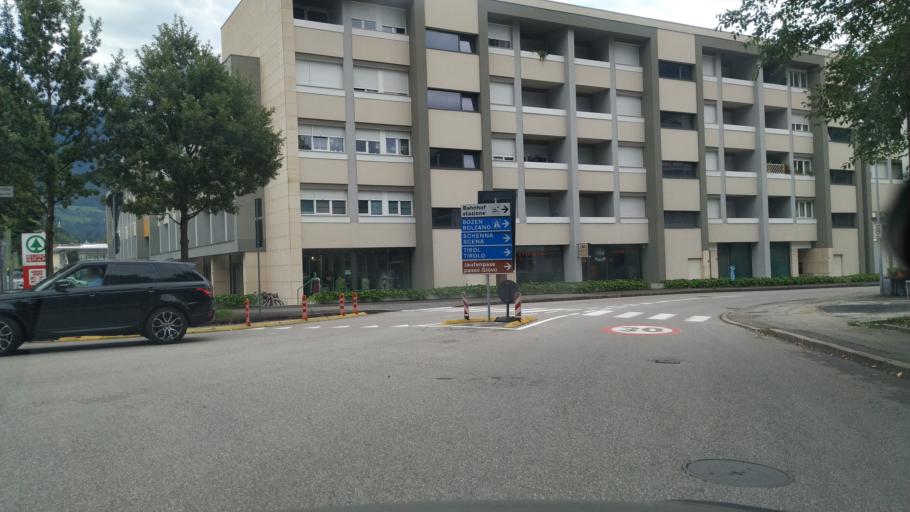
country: IT
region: Trentino-Alto Adige
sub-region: Bolzano
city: Merano
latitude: 46.6767
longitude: 11.1486
